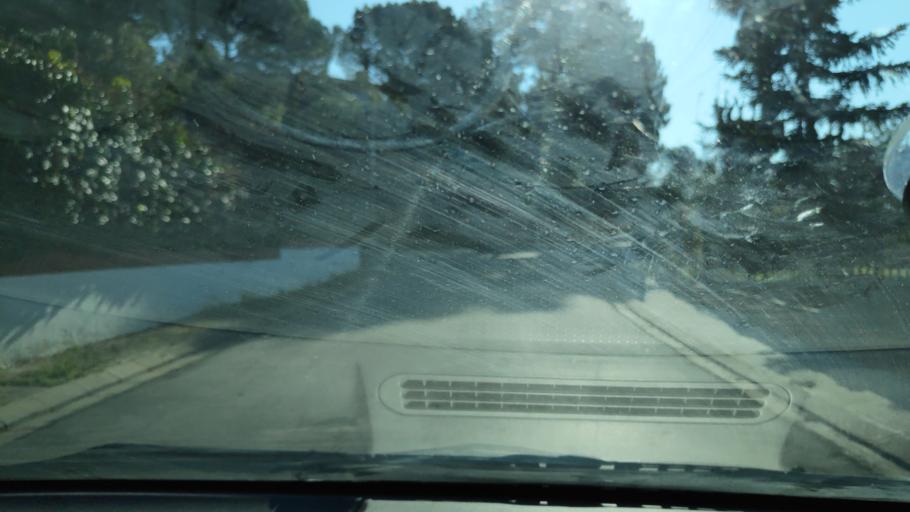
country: ES
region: Catalonia
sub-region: Provincia de Barcelona
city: Sant Cugat del Valles
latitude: 41.4999
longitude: 2.0787
